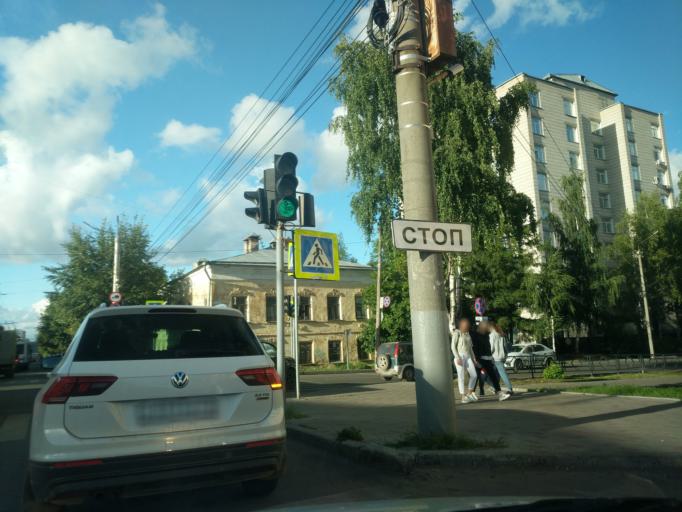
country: RU
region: Kirov
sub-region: Kirovo-Chepetskiy Rayon
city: Kirov
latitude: 58.5961
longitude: 49.6818
